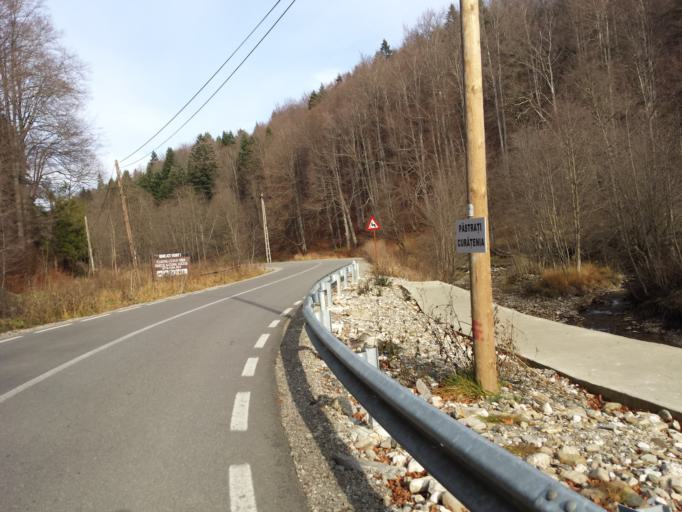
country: RO
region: Prahova
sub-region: Oras Azuga
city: Azuga
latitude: 45.4269
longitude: 25.5375
